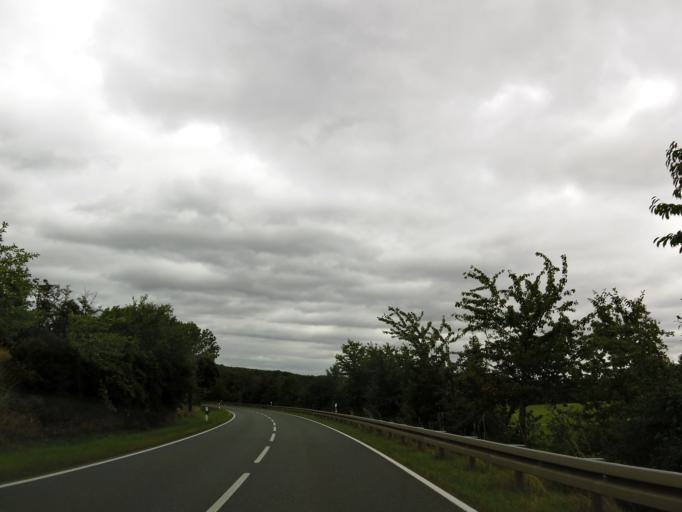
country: DE
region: Saxony-Anhalt
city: Teuchern
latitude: 51.1122
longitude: 12.0195
